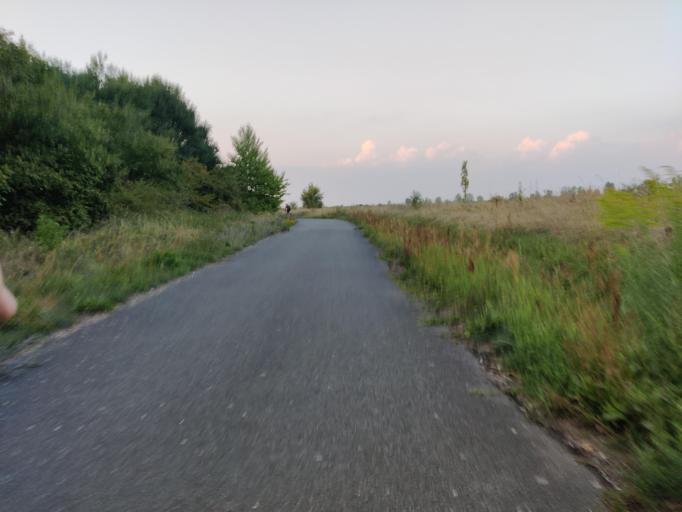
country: DE
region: Saxony
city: Zschortau
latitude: 51.4661
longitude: 12.3211
